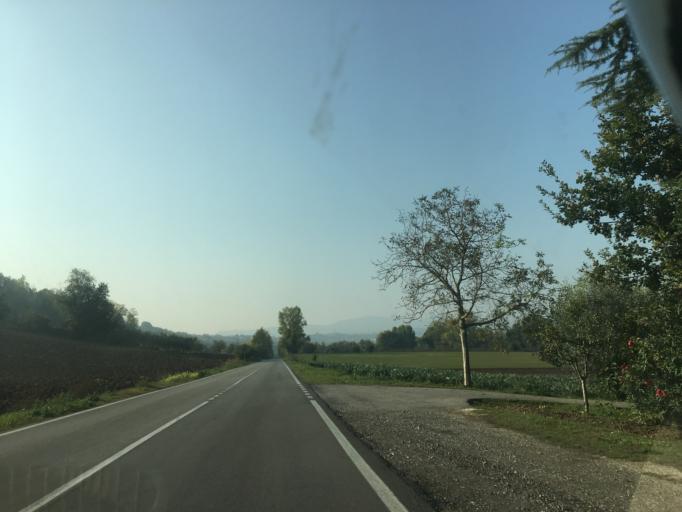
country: IT
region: Emilia-Romagna
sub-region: Provincia di Rimini
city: Ospedaletto
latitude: 43.9679
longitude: 12.5734
